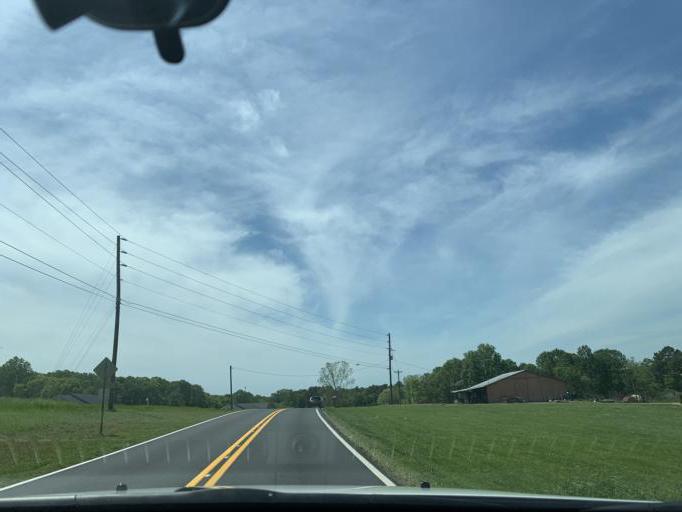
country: US
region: Georgia
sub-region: Forsyth County
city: Cumming
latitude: 34.2643
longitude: -84.0491
